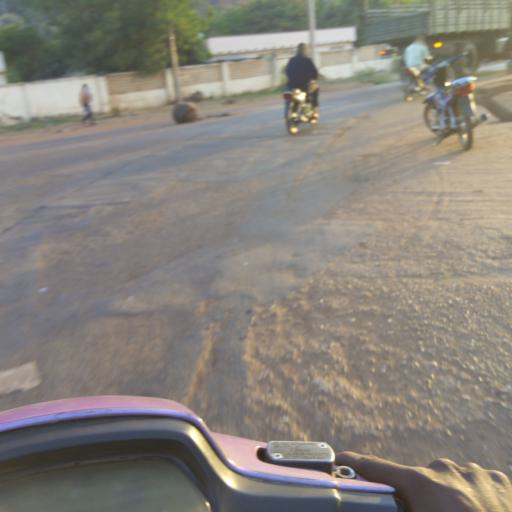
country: ML
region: Bamako
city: Bamako
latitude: 12.6561
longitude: -8.0112
